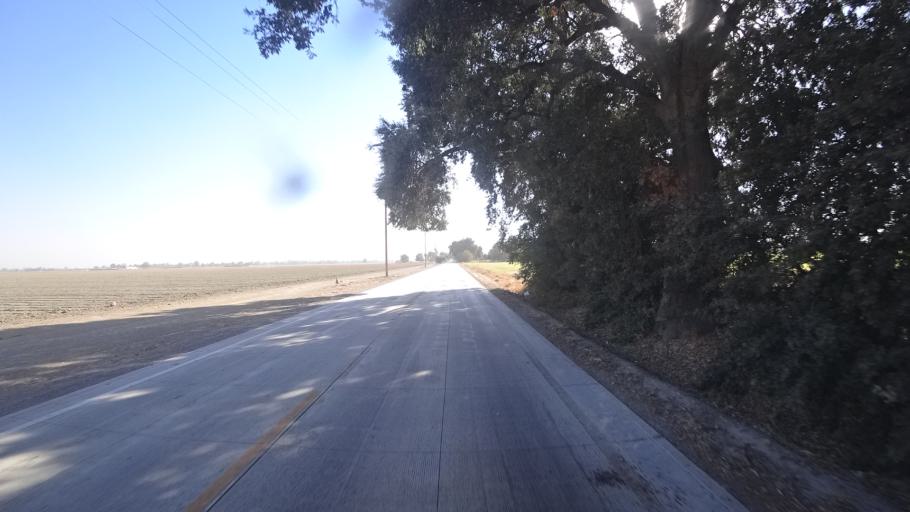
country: US
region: California
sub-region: Yolo County
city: Woodland
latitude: 38.7474
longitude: -121.7757
